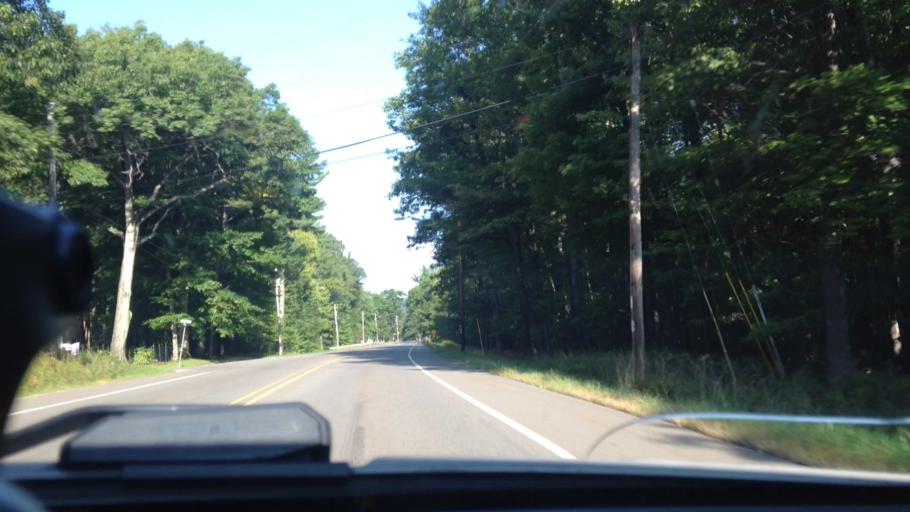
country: US
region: Michigan
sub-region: Dickinson County
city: Quinnesec
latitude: 45.8329
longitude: -88.0054
